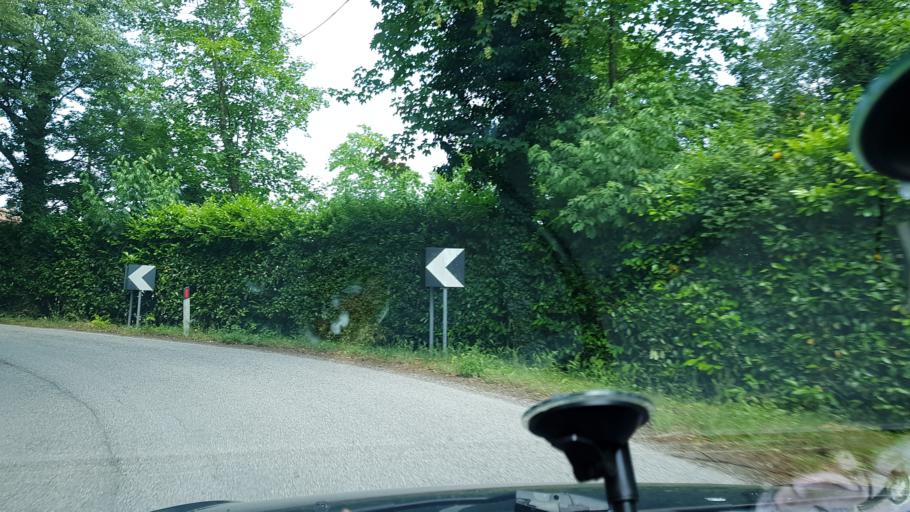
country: IT
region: Friuli Venezia Giulia
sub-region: Provincia di Gorizia
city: Savogna d'Isonzo
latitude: 45.8940
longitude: 13.5735
